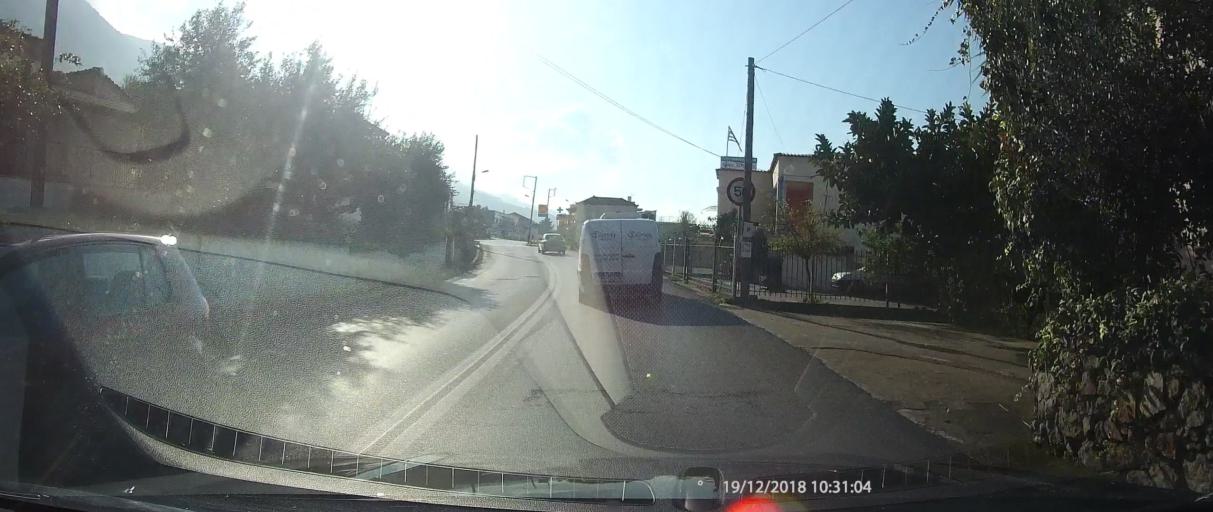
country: GR
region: Peloponnese
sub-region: Nomos Messinias
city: Paralia Vergas
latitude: 37.0113
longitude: 22.1546
